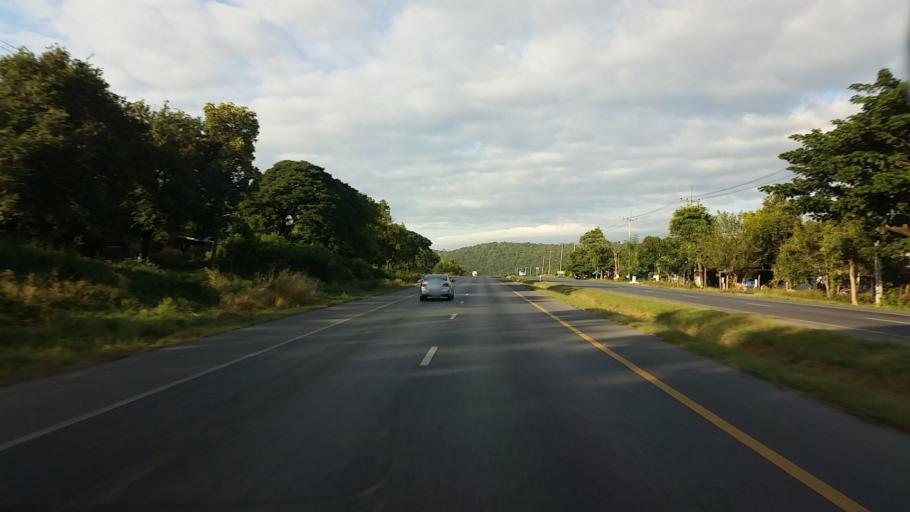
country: TH
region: Lop Buri
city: Phatthana Nikhom
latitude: 14.9821
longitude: 100.9156
